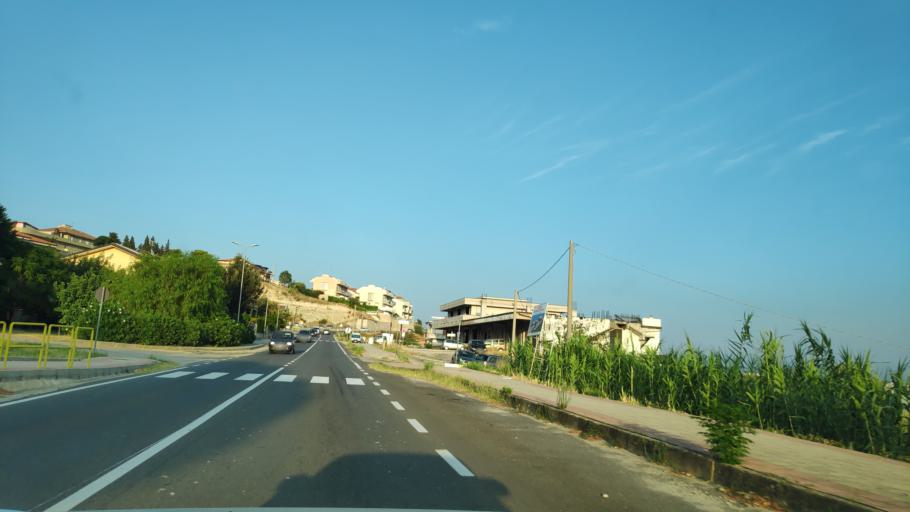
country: IT
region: Calabria
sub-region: Provincia di Catanzaro
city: Martelli-Laganosa
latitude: 38.6792
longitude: 16.5340
